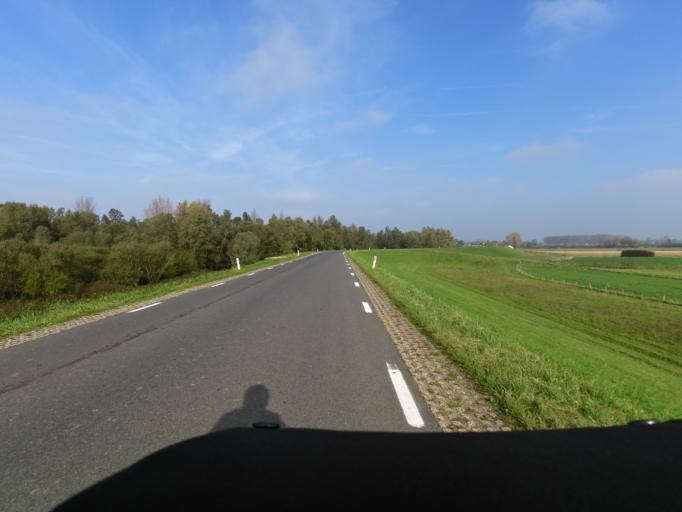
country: DE
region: North Rhine-Westphalia
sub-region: Regierungsbezirk Dusseldorf
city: Kranenburg
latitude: 51.8543
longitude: 5.9910
